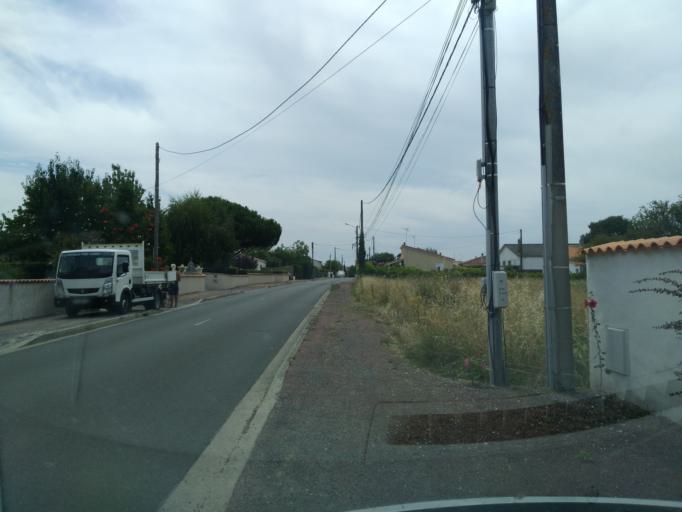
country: FR
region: Poitou-Charentes
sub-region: Departement de la Charente-Maritime
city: Vaux-sur-Mer
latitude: 45.6600
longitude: -1.0746
